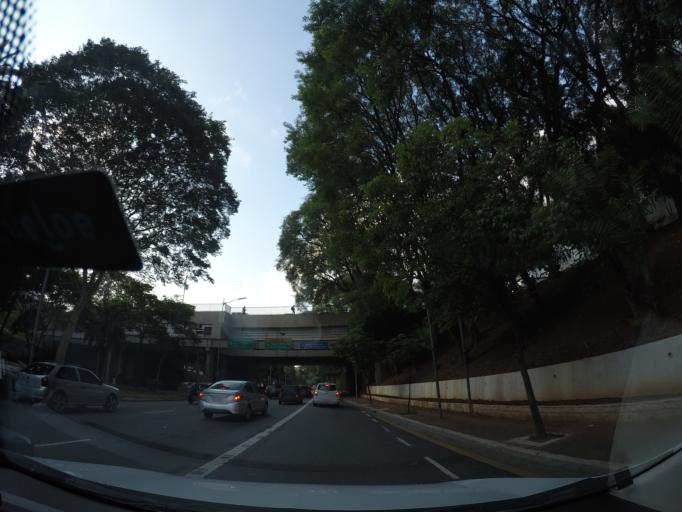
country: BR
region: Sao Paulo
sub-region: Sao Paulo
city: Sao Paulo
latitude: -23.5644
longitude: -46.6384
